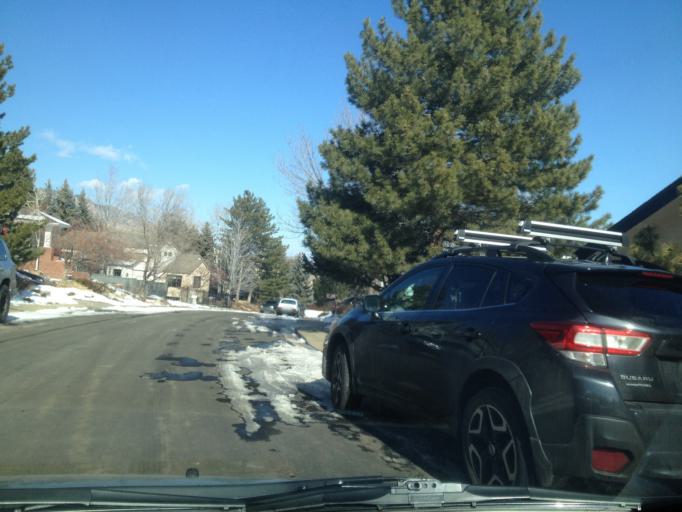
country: US
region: Colorado
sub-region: Boulder County
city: Boulder
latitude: 40.0460
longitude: -105.2937
